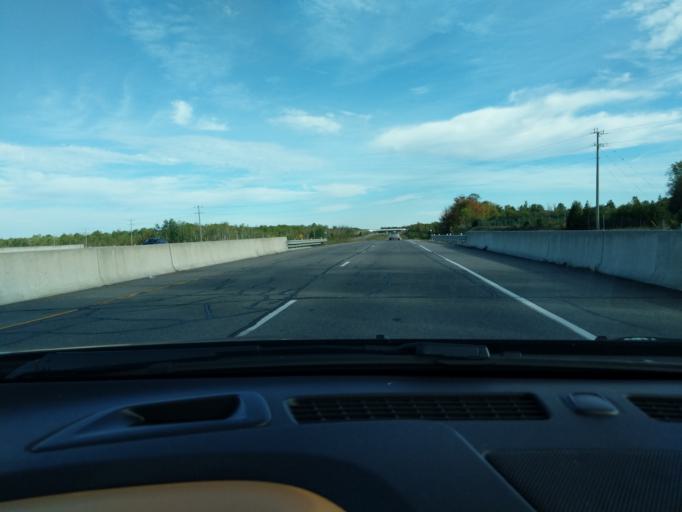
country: CA
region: Ontario
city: Collingwood
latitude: 44.4753
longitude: -80.1534
